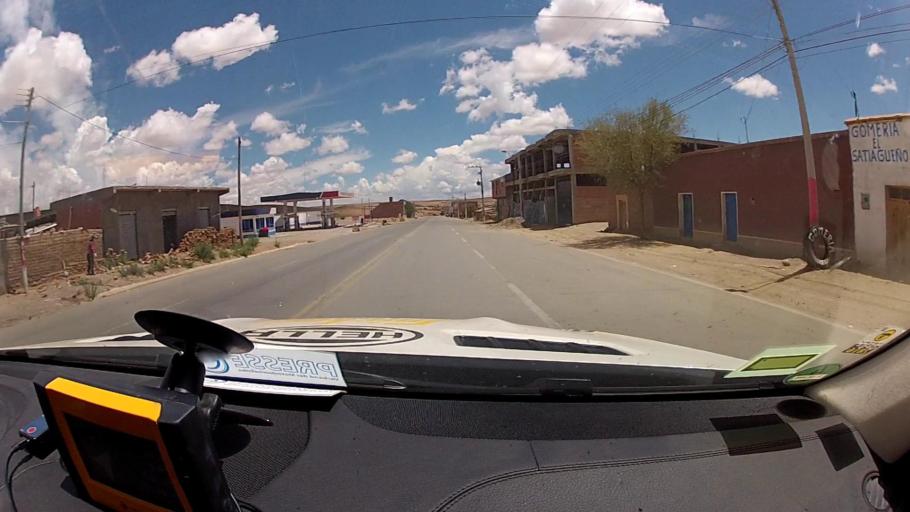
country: BO
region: Potosi
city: Villazon
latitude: -22.0726
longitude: -65.5955
